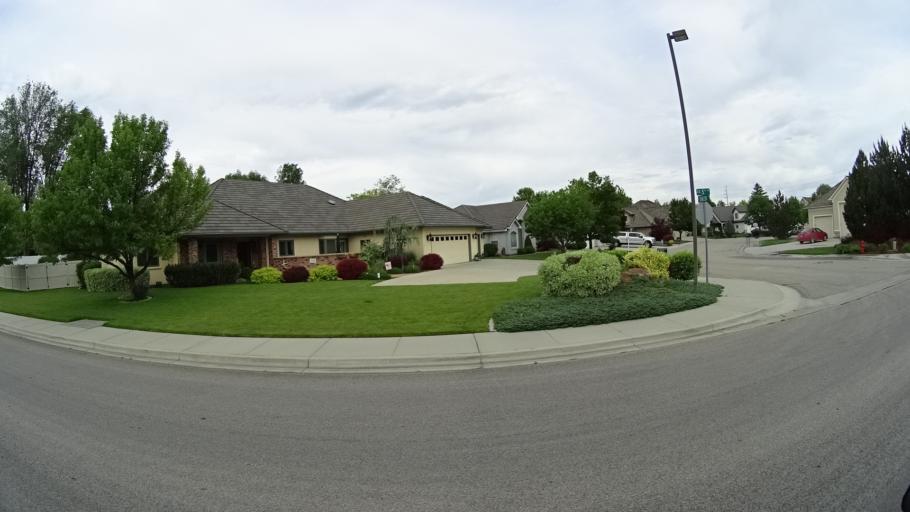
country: US
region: Idaho
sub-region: Ada County
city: Meridian
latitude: 43.5888
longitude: -116.3853
